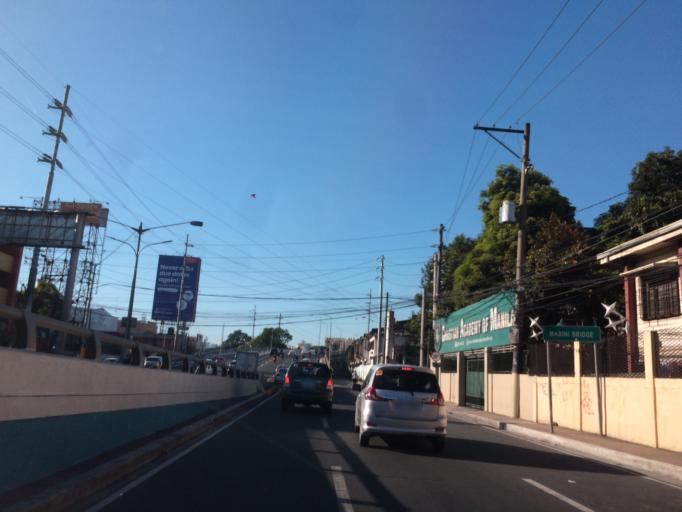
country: PH
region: Metro Manila
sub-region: City of Manila
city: Quiapo
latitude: 14.5989
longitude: 121.0004
